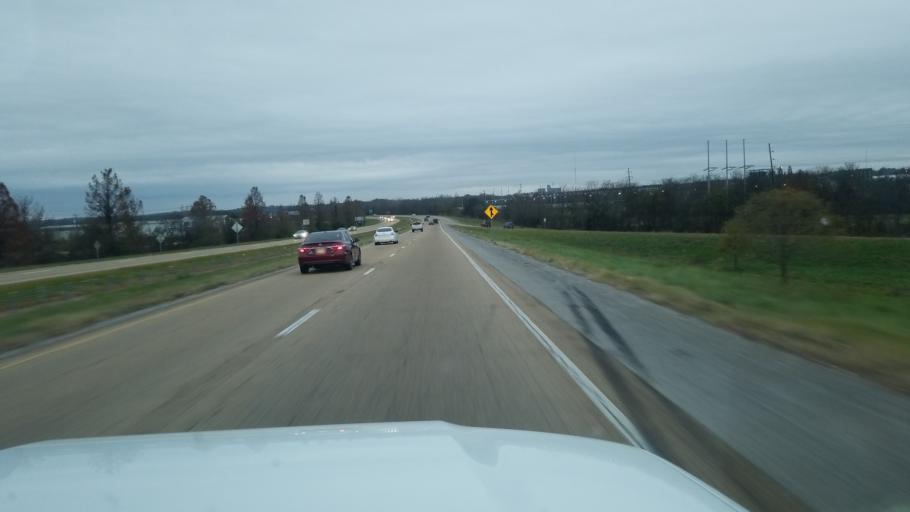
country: US
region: Mississippi
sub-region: Lee County
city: Tupelo
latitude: 34.2349
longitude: -88.7013
